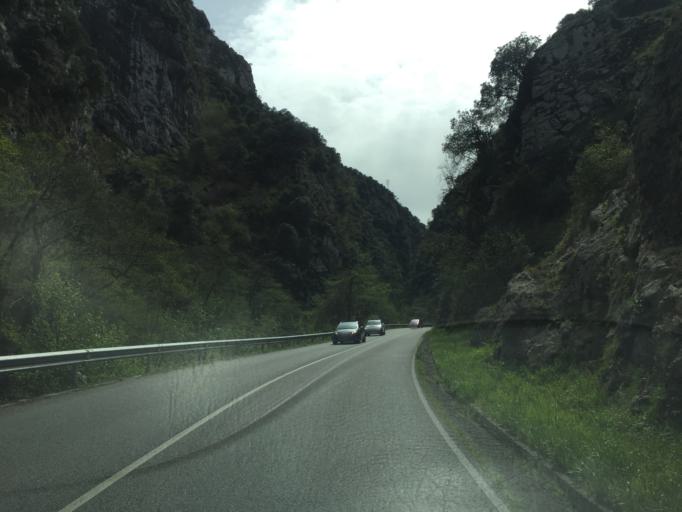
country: ES
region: Asturias
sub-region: Province of Asturias
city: Proaza
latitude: 43.2353
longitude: -6.0314
